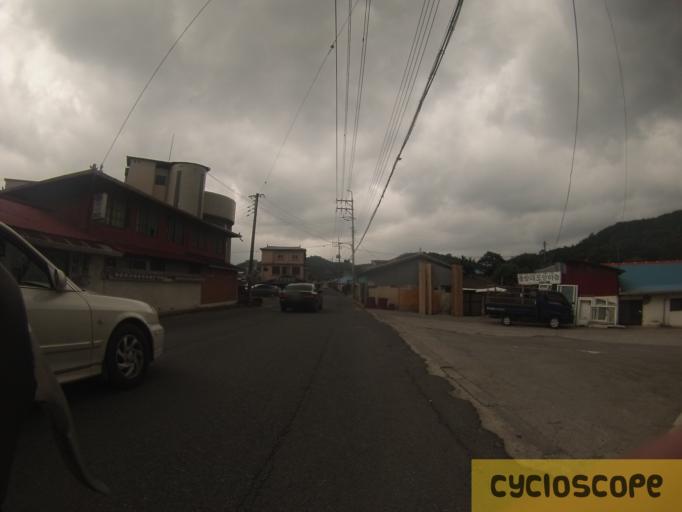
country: KR
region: Chungcheongnam-do
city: Hongsung
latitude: 36.5388
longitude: 126.7738
